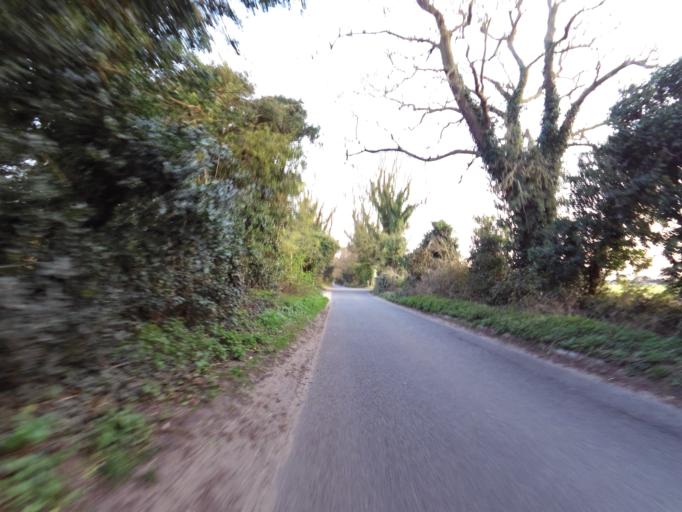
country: GB
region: England
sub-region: Suffolk
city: Kesgrave
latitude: 52.0329
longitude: 1.2378
